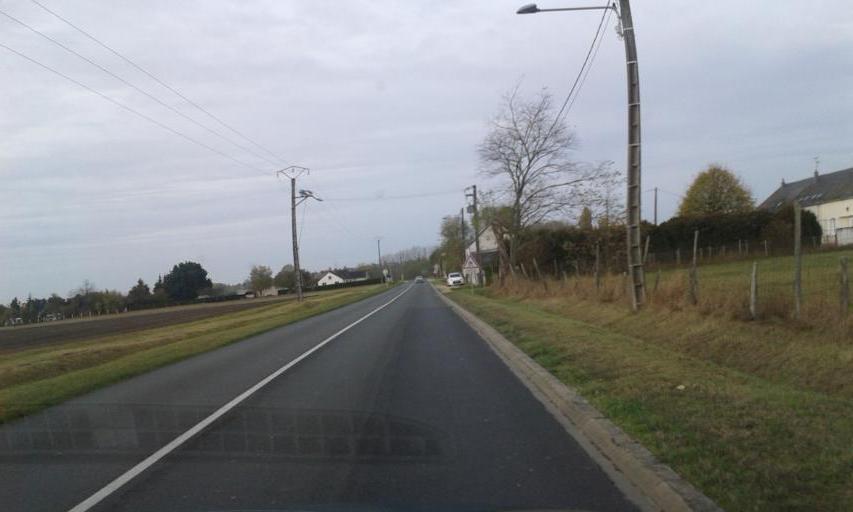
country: FR
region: Centre
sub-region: Departement du Loiret
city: Beaugency
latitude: 47.7762
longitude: 1.6530
